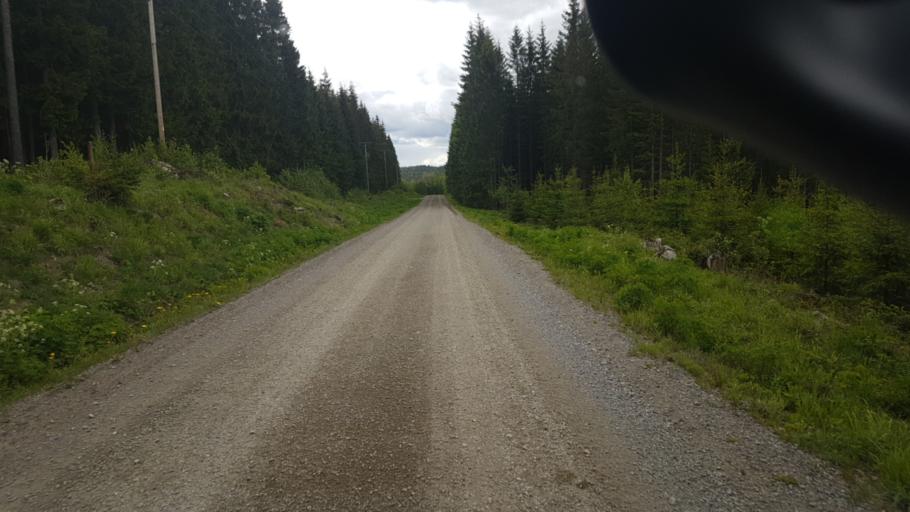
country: SE
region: Vaermland
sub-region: Arvika Kommun
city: Arvika
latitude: 59.8482
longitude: 12.7224
